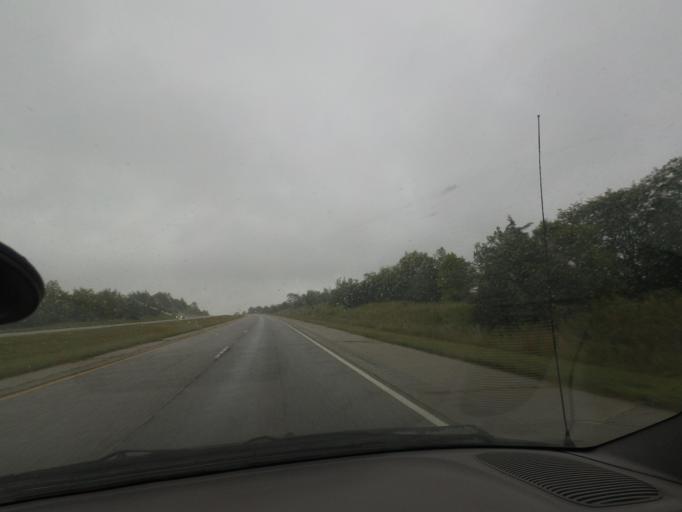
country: US
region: Illinois
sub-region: Pike County
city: Barry
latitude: 39.6925
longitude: -90.9955
